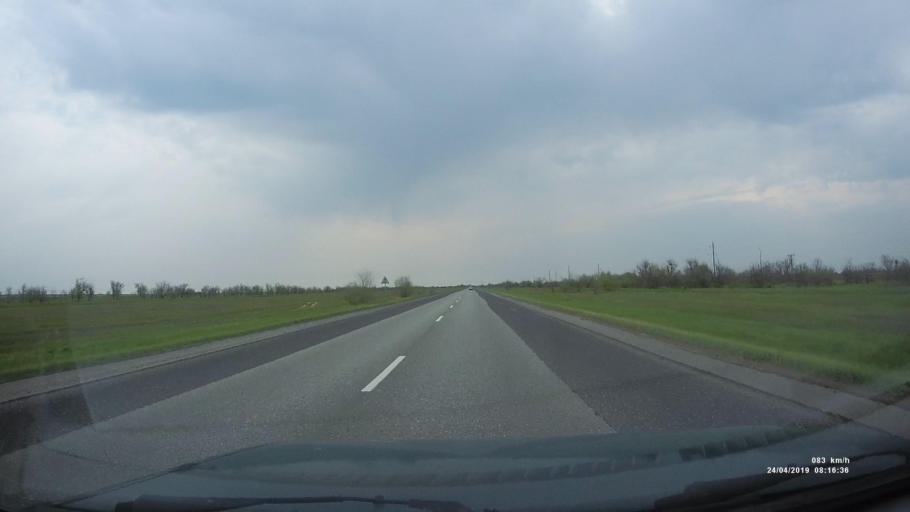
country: RU
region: Kalmykiya
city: Priyutnoye
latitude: 46.0988
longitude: 43.6151
